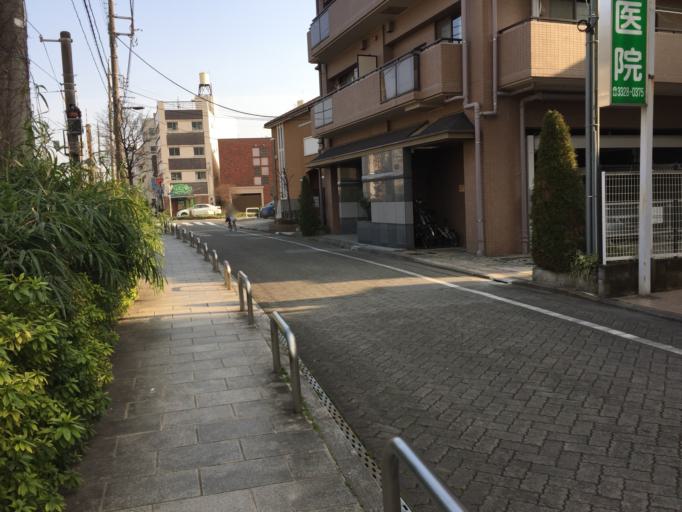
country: JP
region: Tokyo
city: Tokyo
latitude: 35.6584
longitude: 139.6424
